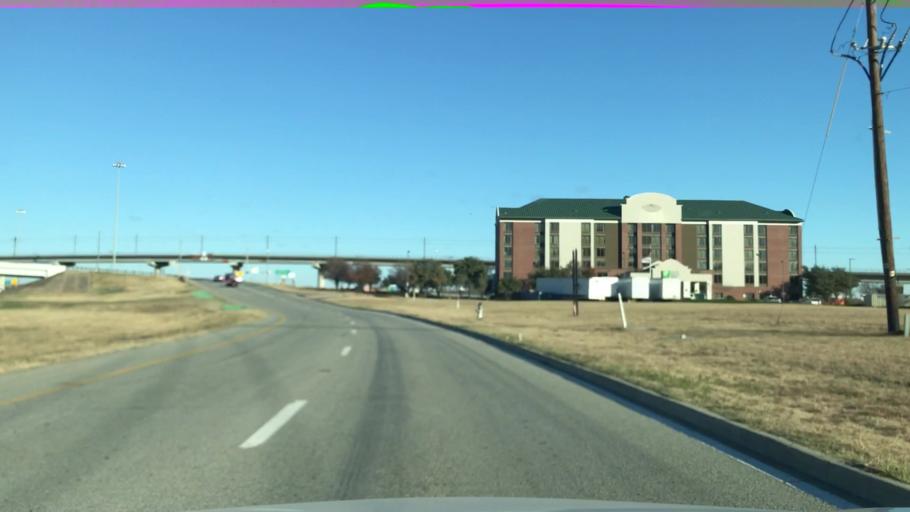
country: US
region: Texas
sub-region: Dallas County
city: Irving
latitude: 32.8779
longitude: -96.9459
